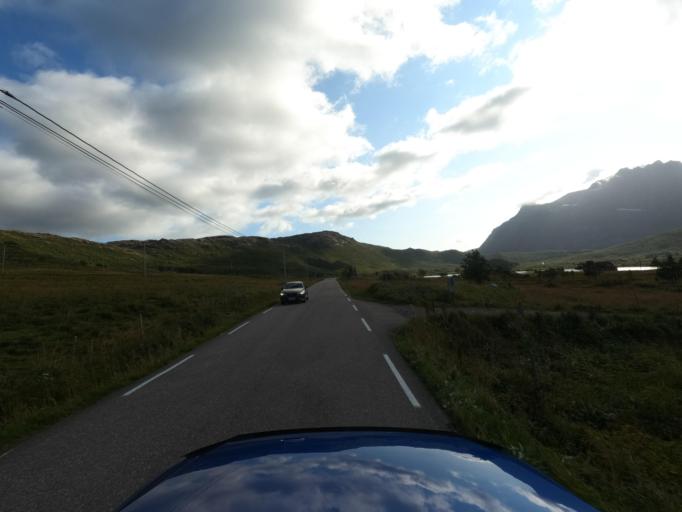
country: NO
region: Nordland
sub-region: Flakstad
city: Ramberg
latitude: 68.0807
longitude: 13.3439
